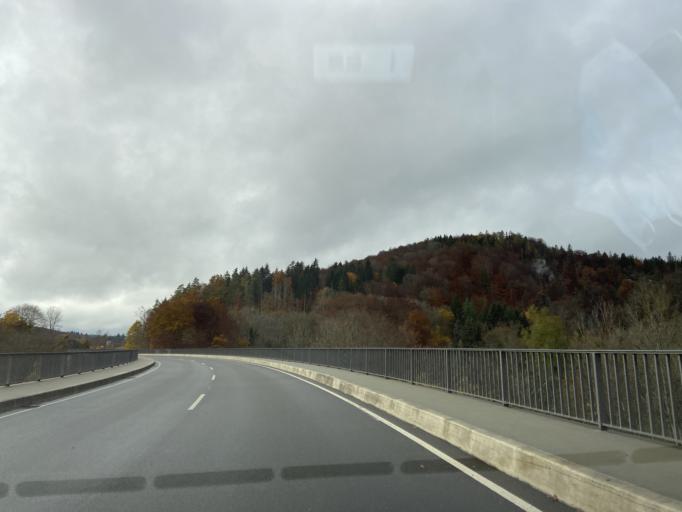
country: DE
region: Baden-Wuerttemberg
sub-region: Tuebingen Region
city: Inzigkofen
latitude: 48.0801
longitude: 9.1537
